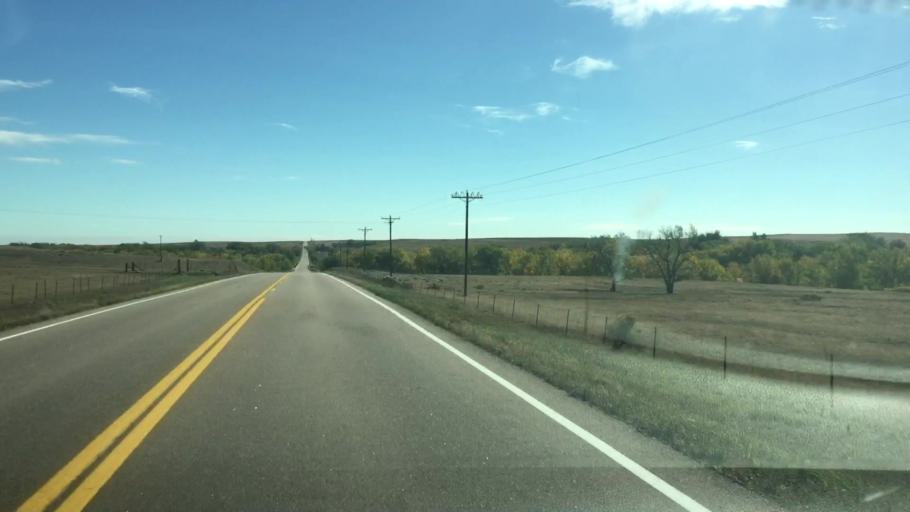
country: US
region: Colorado
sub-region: Elbert County
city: Kiowa
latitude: 39.2736
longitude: -104.1491
